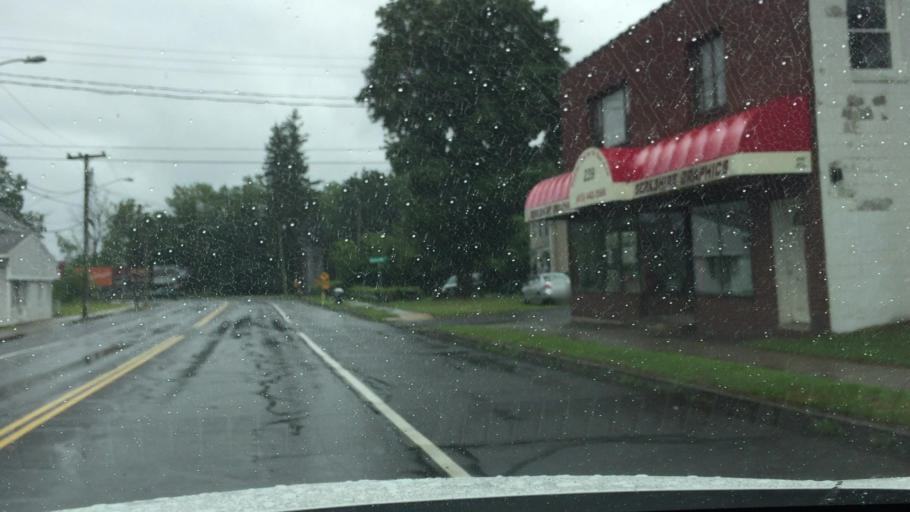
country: US
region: Massachusetts
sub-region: Berkshire County
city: Pittsfield
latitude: 42.4655
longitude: -73.2529
